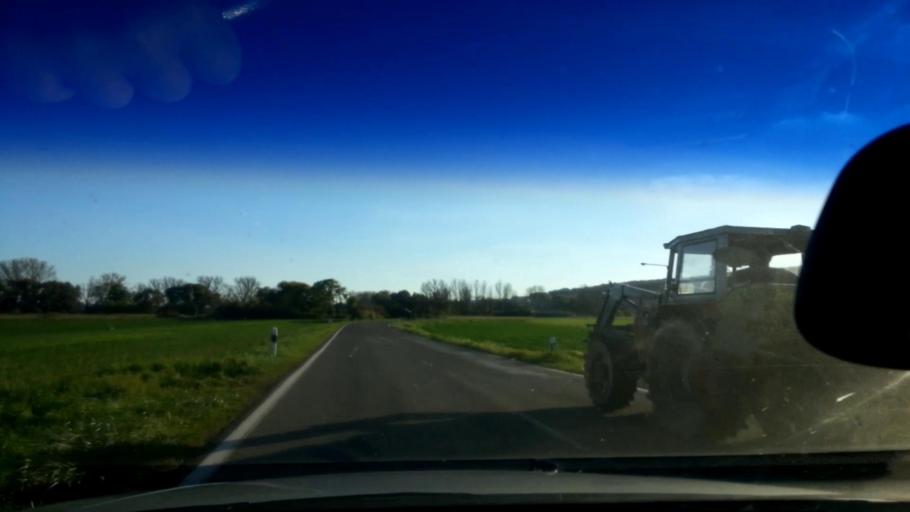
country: DE
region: Bavaria
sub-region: Upper Franconia
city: Rattelsdorf
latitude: 50.0173
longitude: 10.8787
